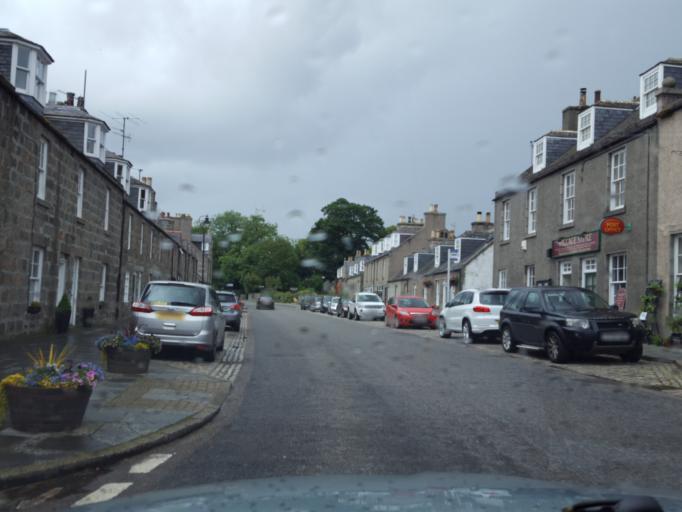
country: GB
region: Scotland
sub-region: Aberdeenshire
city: Torphins
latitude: 57.0862
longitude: -2.6751
